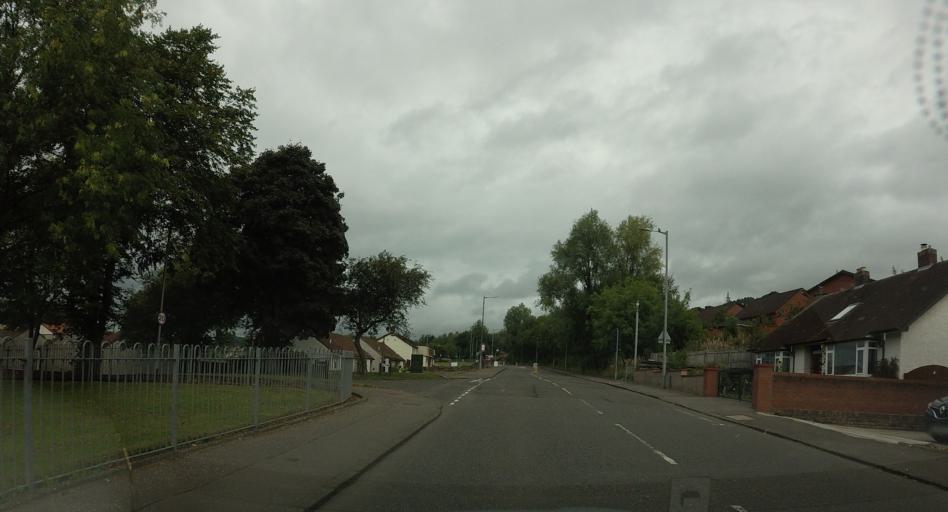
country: GB
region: Scotland
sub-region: Clackmannanshire
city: Alloa
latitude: 56.1287
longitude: -3.7877
